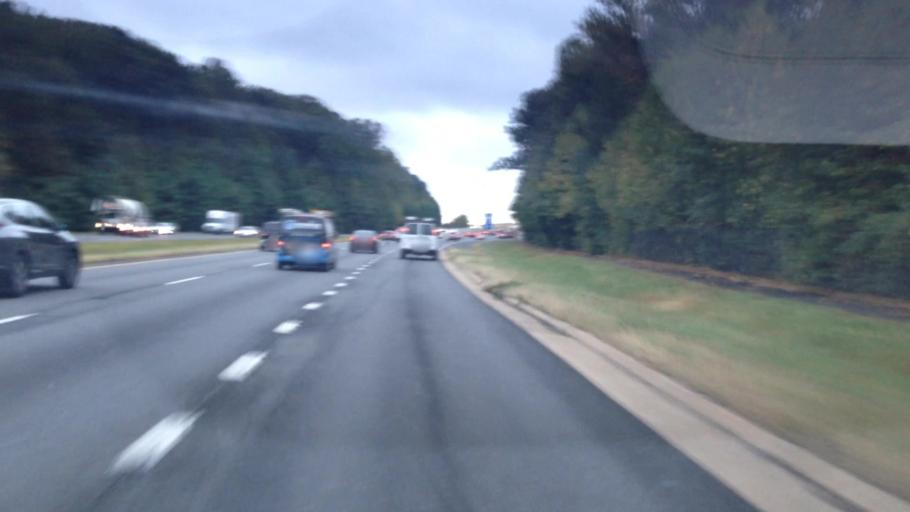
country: US
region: Virginia
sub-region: Fairfax County
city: Greenbriar
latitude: 38.8390
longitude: -77.3738
